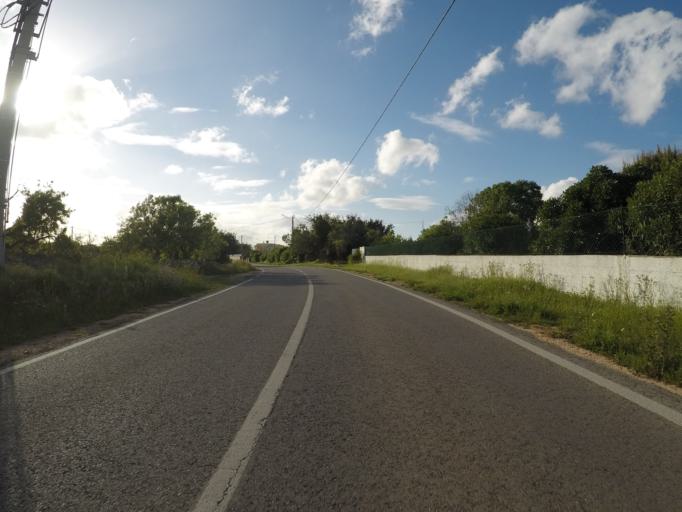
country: PT
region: Faro
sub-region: Lagoa
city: Carvoeiro
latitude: 37.0925
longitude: -8.4305
